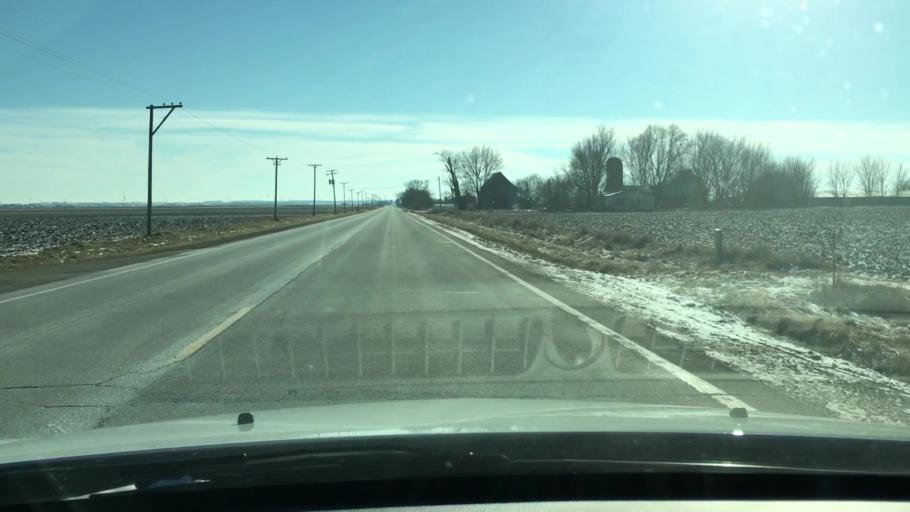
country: US
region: Illinois
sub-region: Ogle County
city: Rochelle
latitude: 41.8250
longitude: -89.0832
